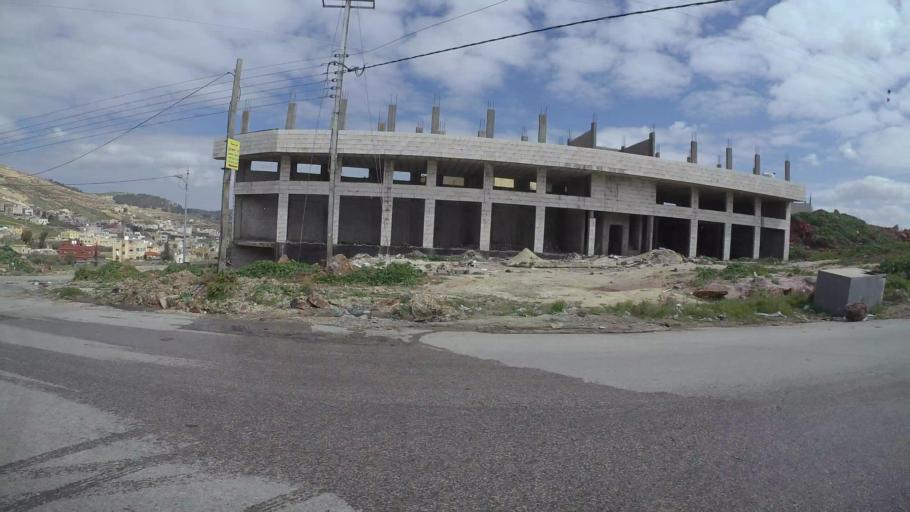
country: JO
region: Amman
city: Al Jubayhah
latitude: 32.0614
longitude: 35.8091
